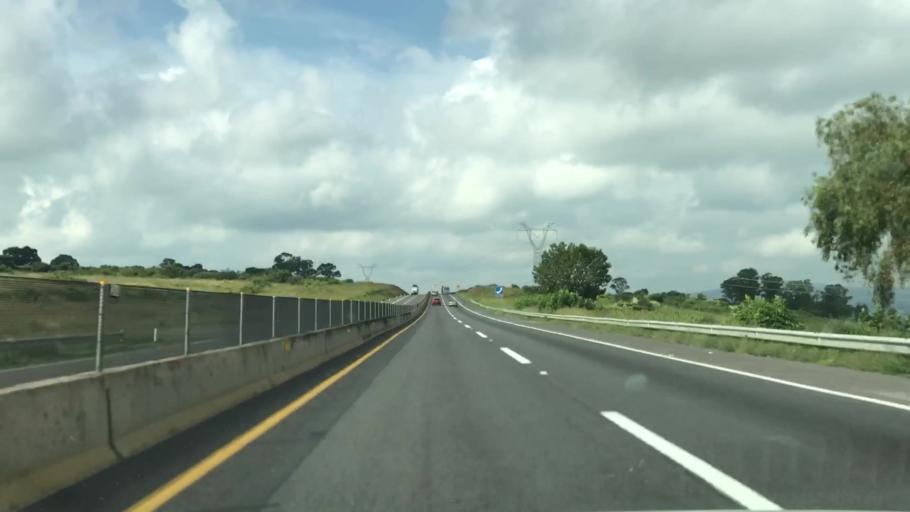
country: MX
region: Jalisco
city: Valle de Guadalupe
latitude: 20.9520
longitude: -102.6431
